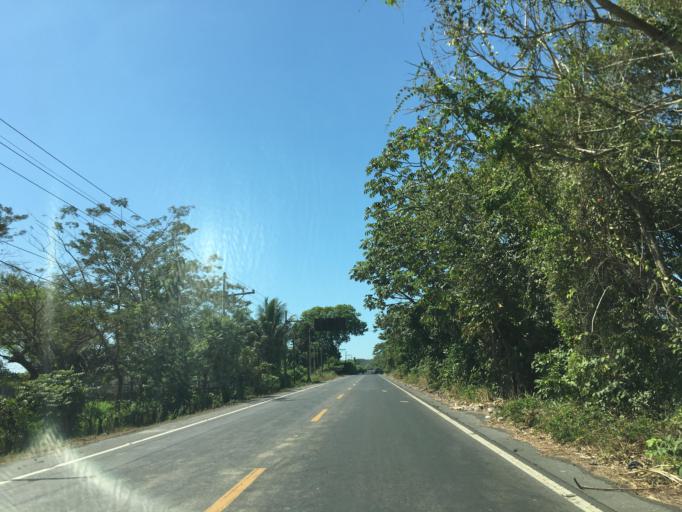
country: GT
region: Escuintla
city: Puerto San Jose
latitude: 14.0166
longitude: -90.8917
